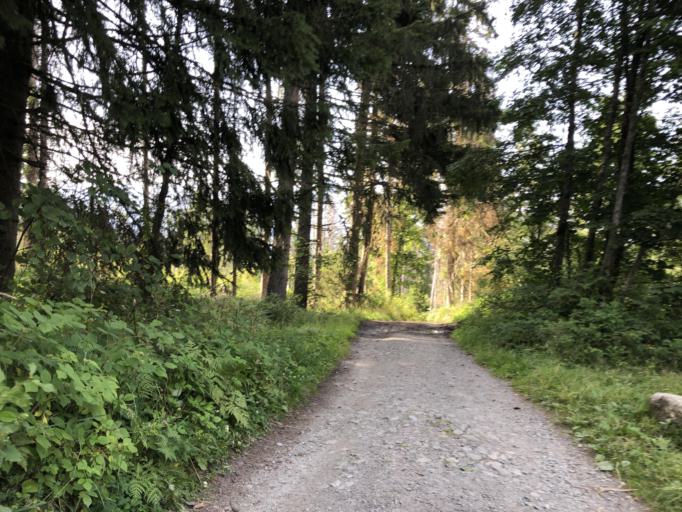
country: FR
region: Rhone-Alpes
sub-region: Departement de la Haute-Savoie
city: Combloux
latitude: 45.8783
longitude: 6.6595
